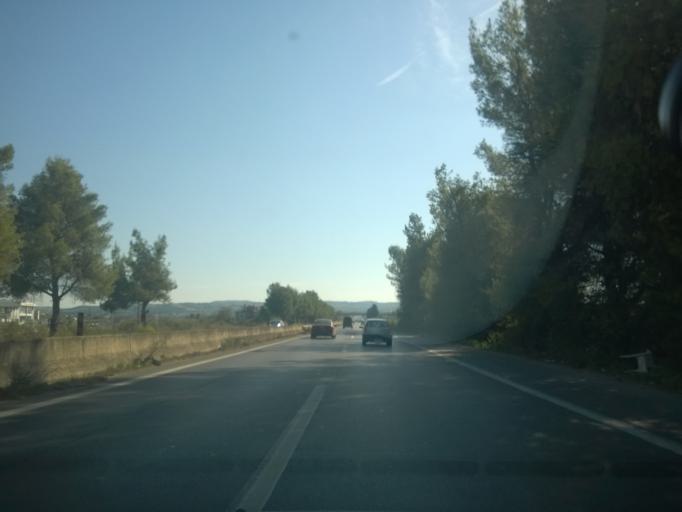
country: GR
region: Central Macedonia
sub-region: Nomos Thessalonikis
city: Thermi
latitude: 40.5183
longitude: 23.0104
